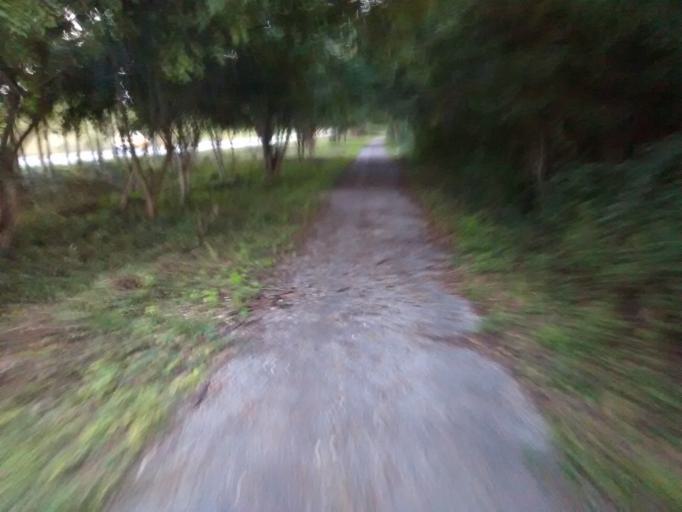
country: MX
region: Yucatan
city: Valladolid
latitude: 20.6945
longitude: -88.2276
